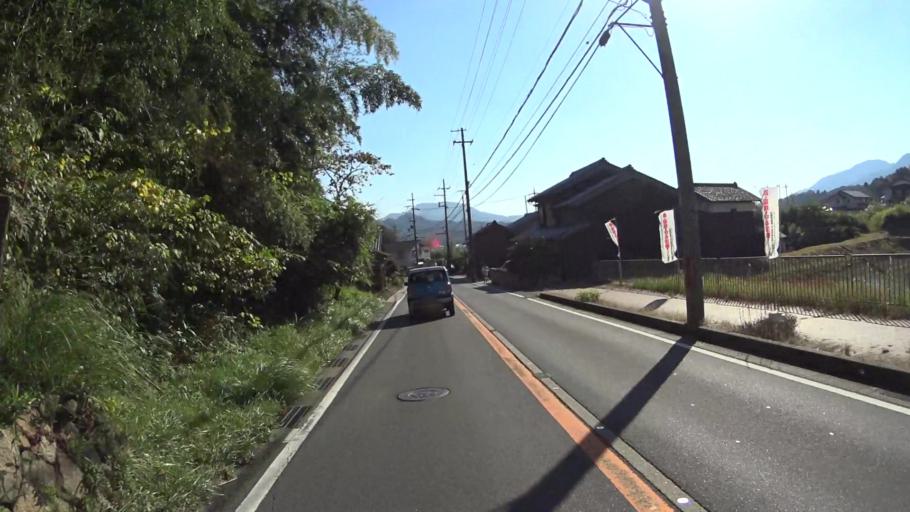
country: JP
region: Kyoto
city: Miyazu
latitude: 35.6162
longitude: 135.0608
